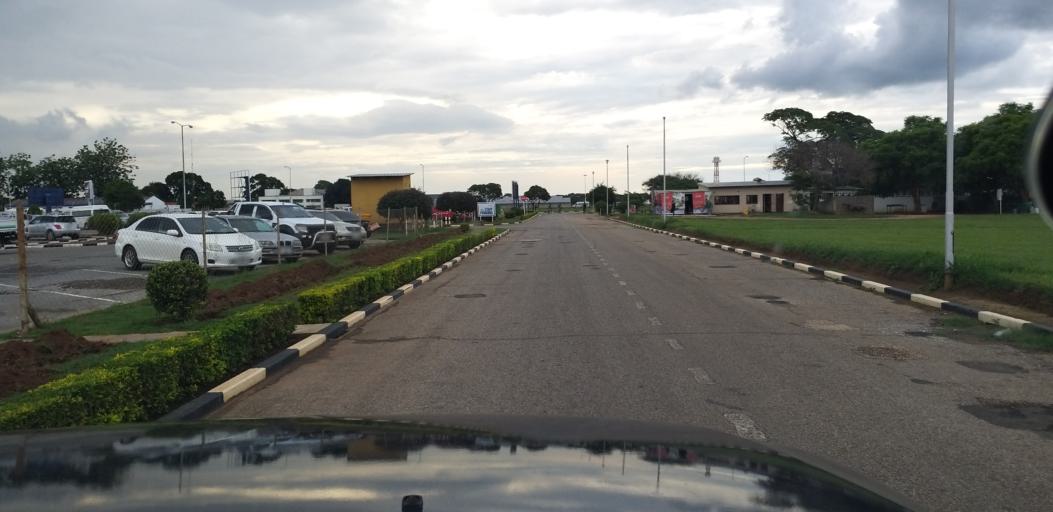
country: ZM
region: Lusaka
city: Lusaka
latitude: -15.3223
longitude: 28.4468
